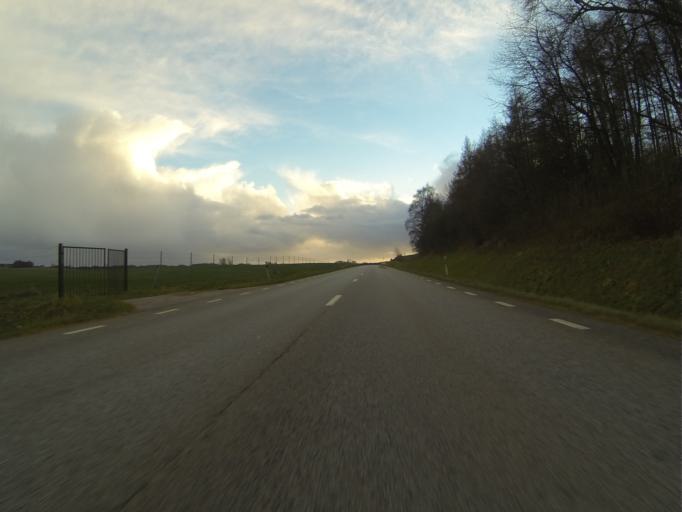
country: SE
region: Skane
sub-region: Trelleborgs Kommun
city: Anderslov
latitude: 55.5215
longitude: 13.3344
